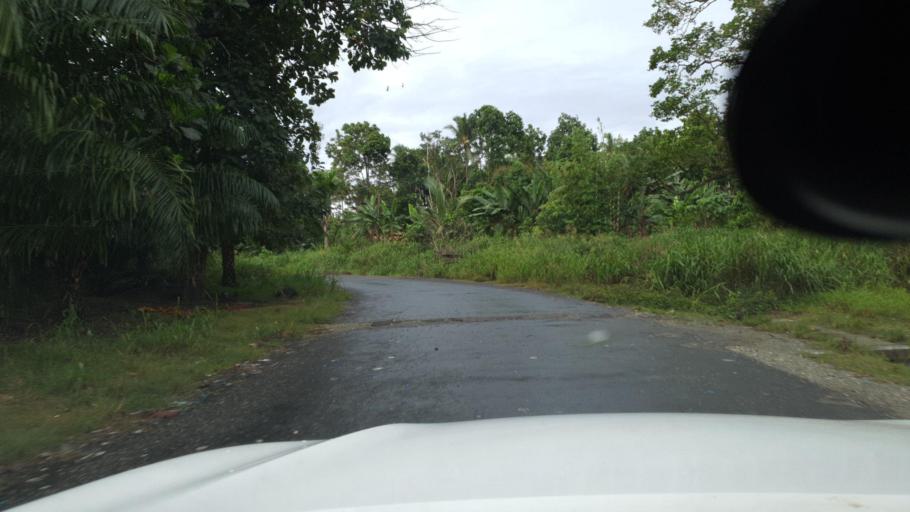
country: SB
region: Guadalcanal
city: Honiara
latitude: -9.4793
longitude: 160.3595
